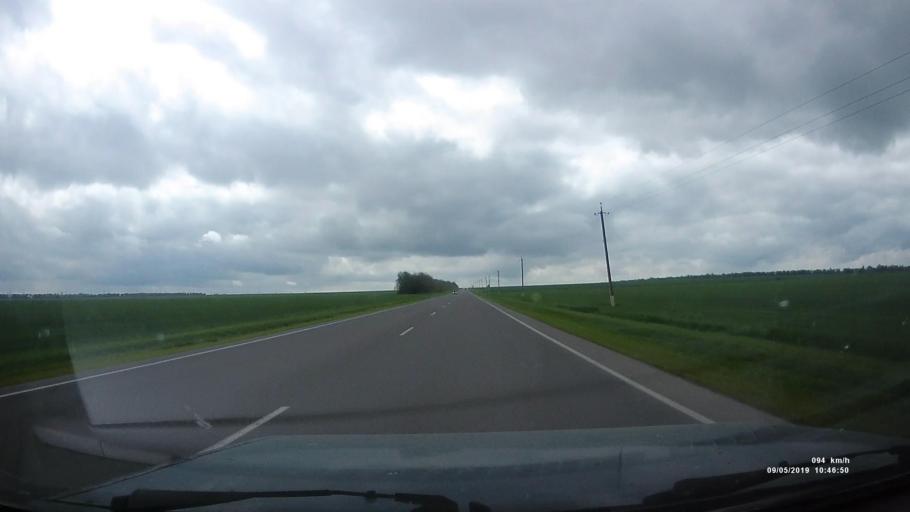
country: RU
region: Rostov
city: Peshkovo
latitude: 46.9790
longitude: 39.3557
